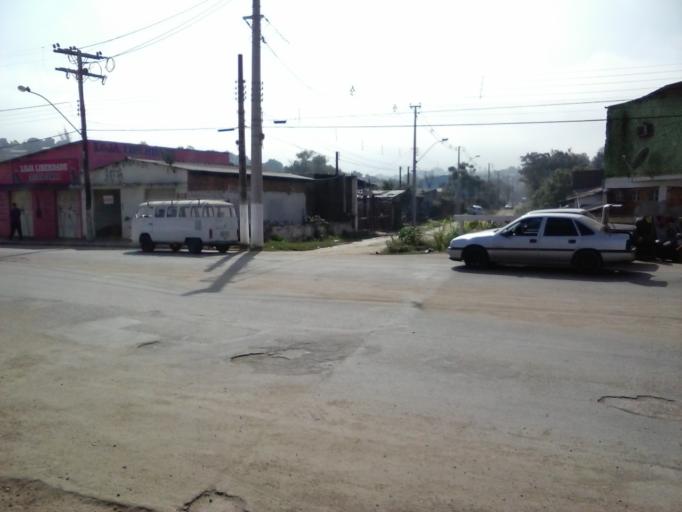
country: BR
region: Rio Grande do Sul
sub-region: Viamao
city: Viamao
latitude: -30.0576
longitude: -51.0808
